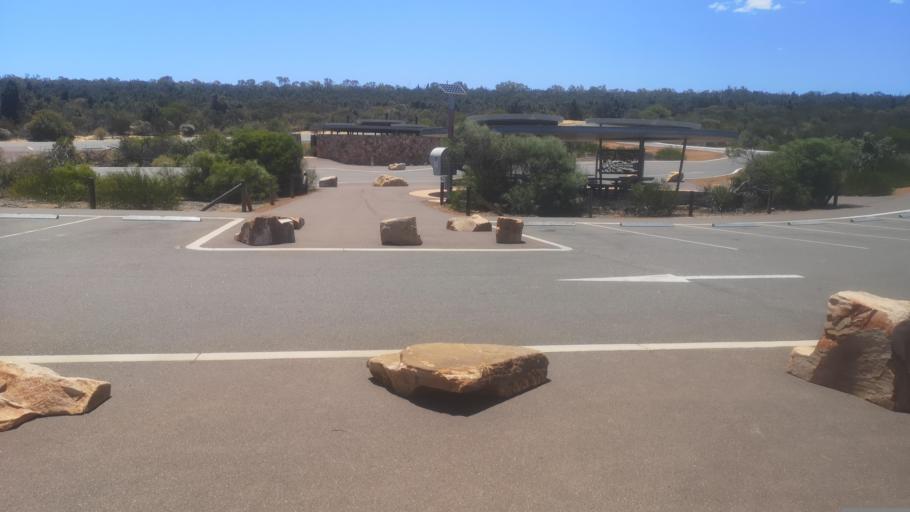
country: AU
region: Western Australia
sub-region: Northampton Shire
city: Kalbarri
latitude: -27.6492
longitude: 114.4555
